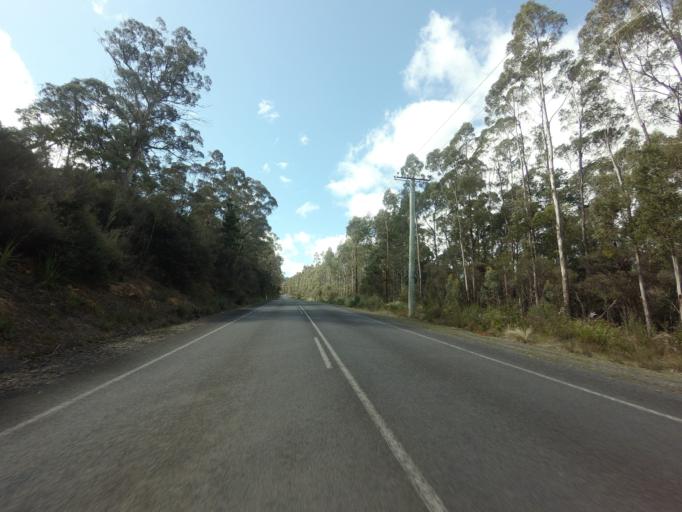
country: AU
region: Tasmania
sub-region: Huon Valley
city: Geeveston
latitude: -43.4149
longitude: 146.9371
